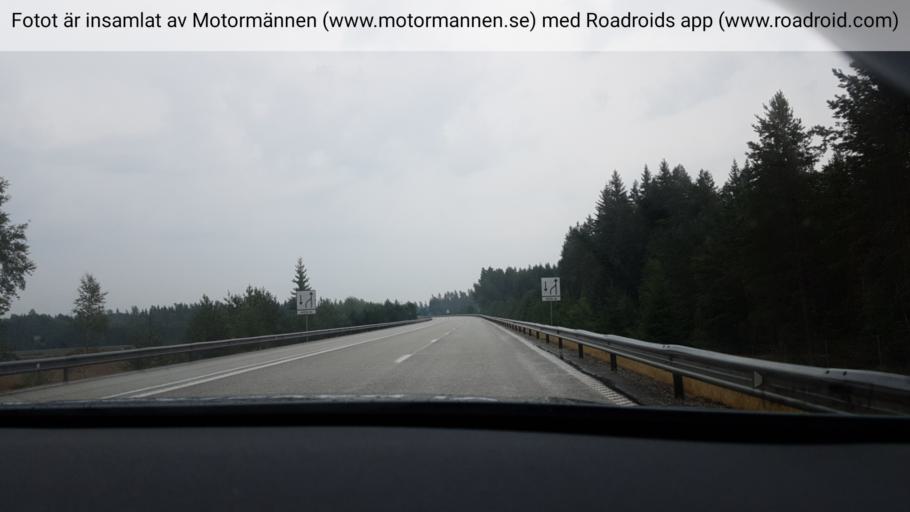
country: SE
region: Joenkoeping
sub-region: Jonkopings Kommun
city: Odensjo
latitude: 57.6209
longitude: 14.1925
